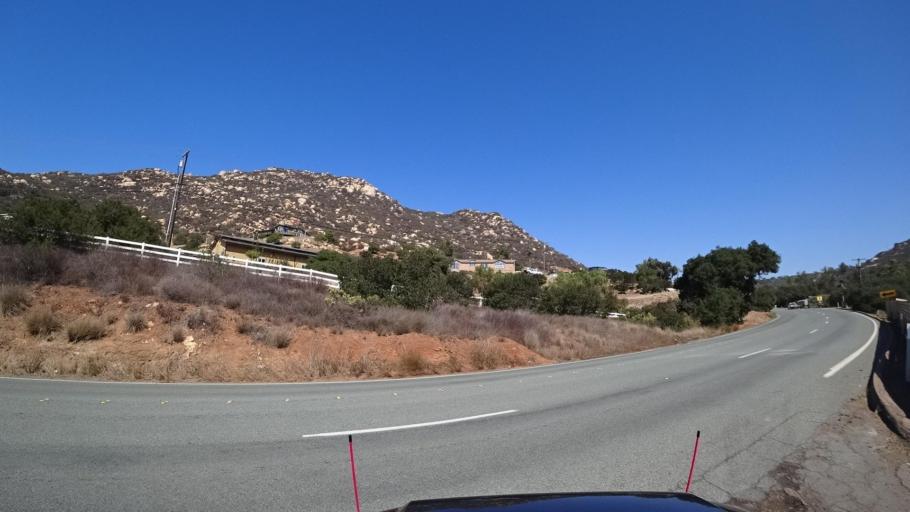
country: US
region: California
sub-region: San Diego County
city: Crest
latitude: 32.8087
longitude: -116.8856
